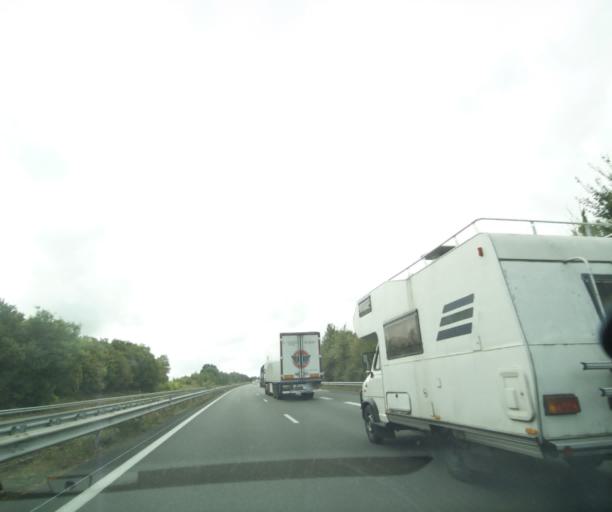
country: FR
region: Poitou-Charentes
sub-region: Departement de la Charente-Maritime
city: Saint-Genis-de-Saintonge
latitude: 45.4365
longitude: -0.6059
